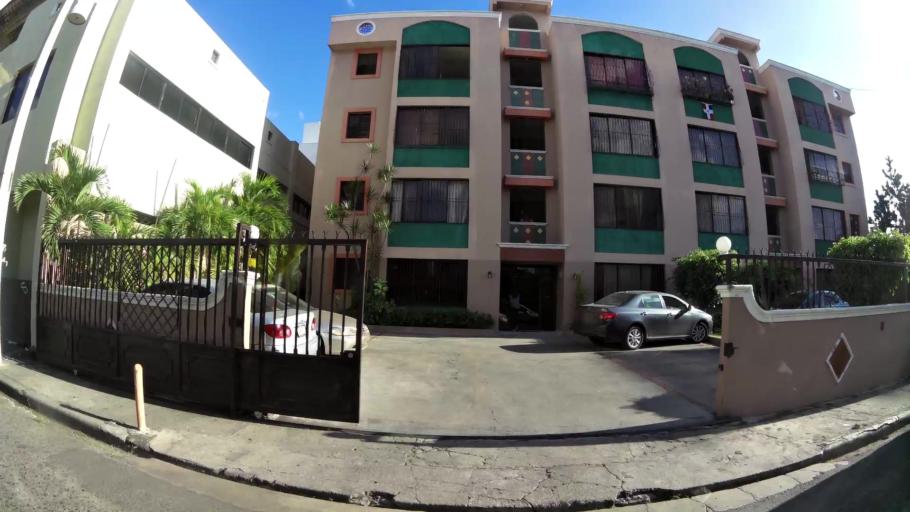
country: DO
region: Santiago
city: Santiago de los Caballeros
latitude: 19.4618
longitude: -70.6892
